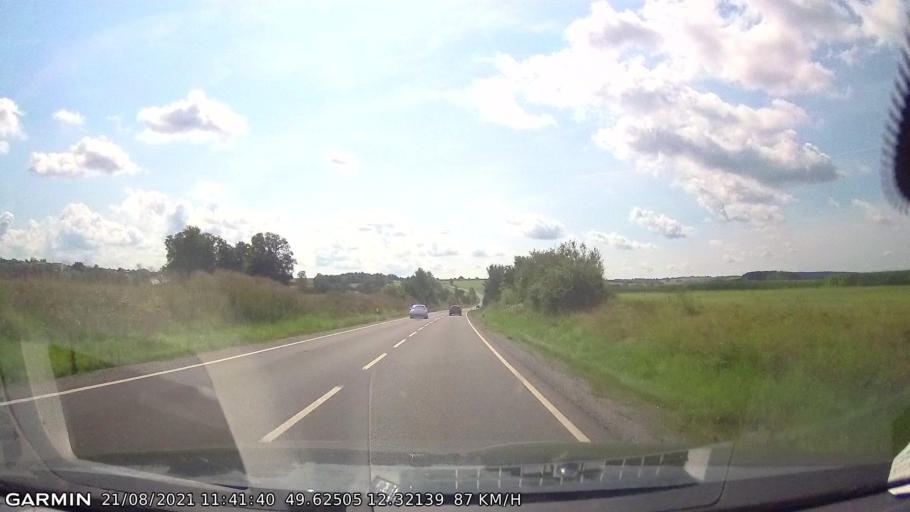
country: DE
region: Bavaria
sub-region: Upper Palatinate
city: Vohenstrauss
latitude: 49.6250
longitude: 12.3214
